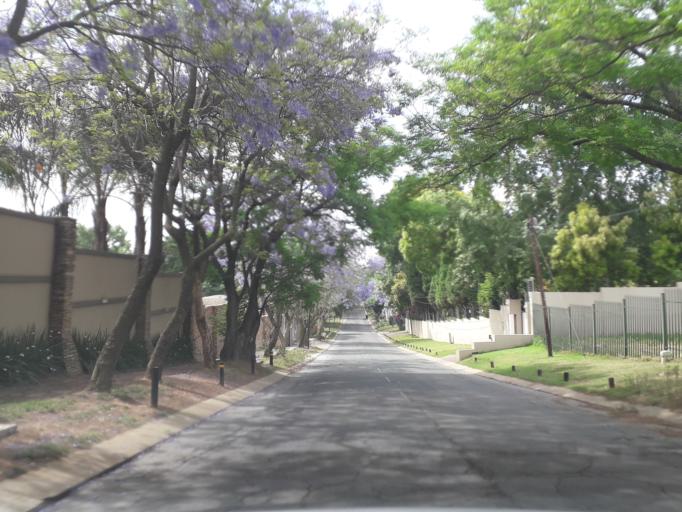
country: ZA
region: Gauteng
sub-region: City of Johannesburg Metropolitan Municipality
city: Diepsloot
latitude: -26.0656
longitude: 28.0189
